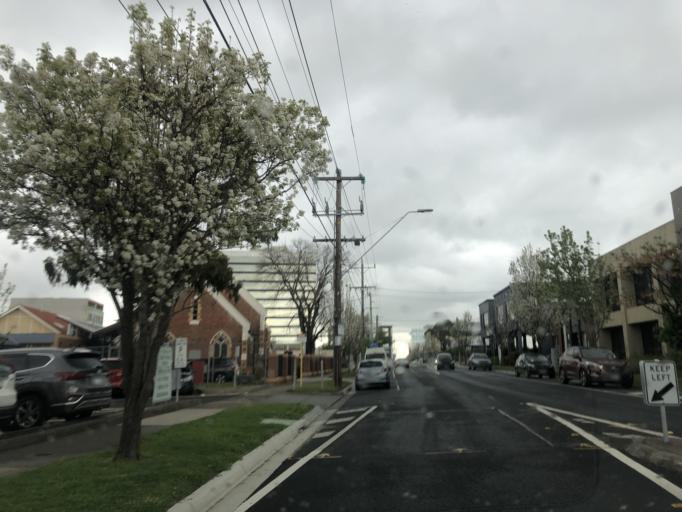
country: AU
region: Victoria
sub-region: Greater Dandenong
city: Dandenong
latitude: -37.9853
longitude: 145.2114
